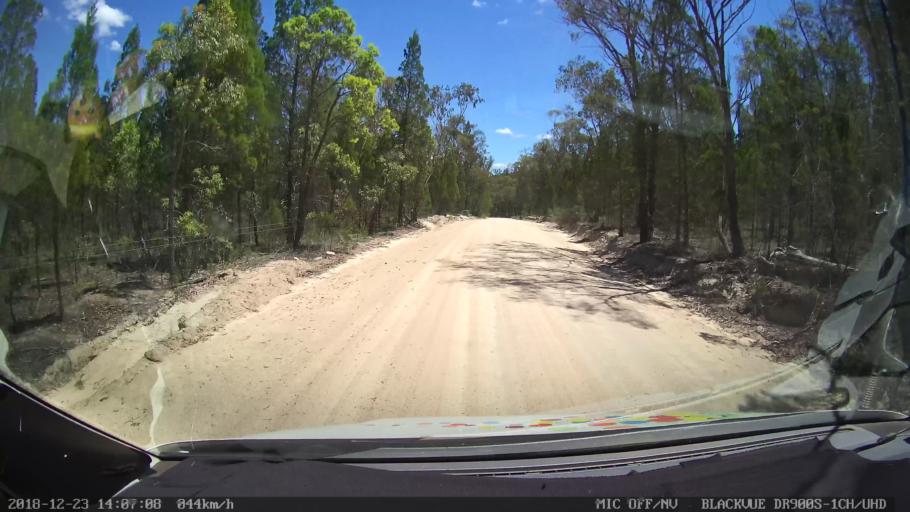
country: AU
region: New South Wales
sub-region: Tamworth Municipality
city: Manilla
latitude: -30.6341
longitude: 151.0731
